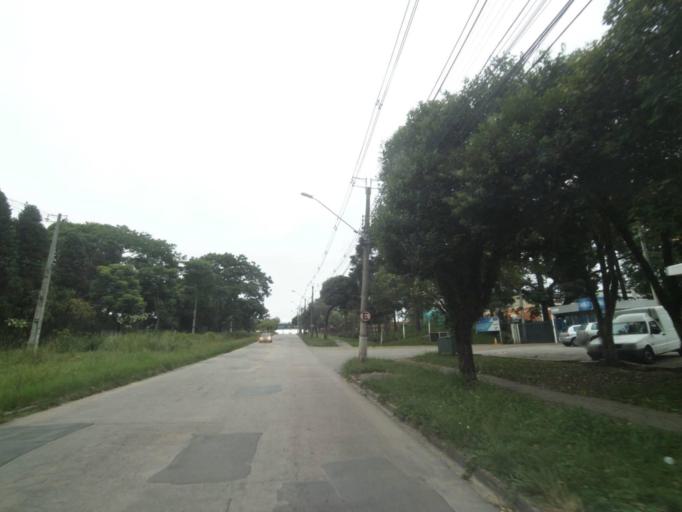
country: BR
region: Parana
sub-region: Araucaria
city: Araucaria
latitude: -25.5366
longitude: -49.3182
